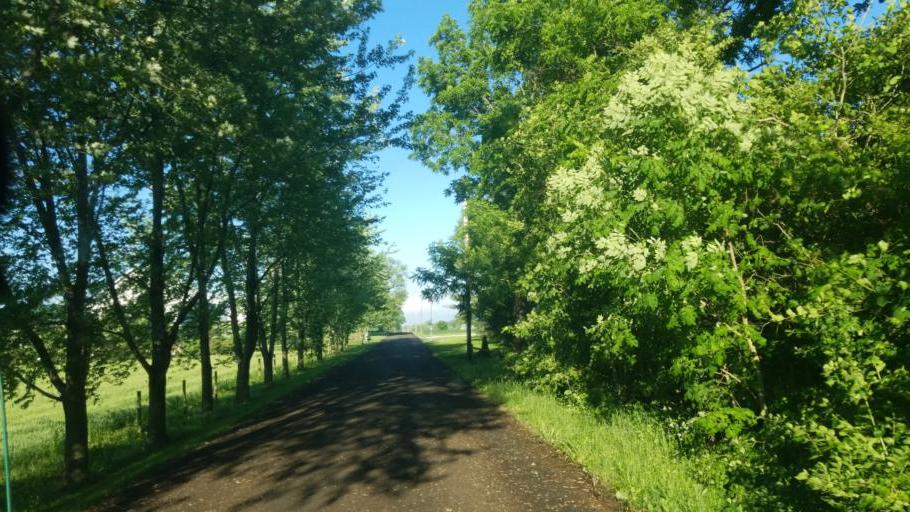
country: US
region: Indiana
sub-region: Elkhart County
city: Nappanee
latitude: 41.4191
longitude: -86.0722
